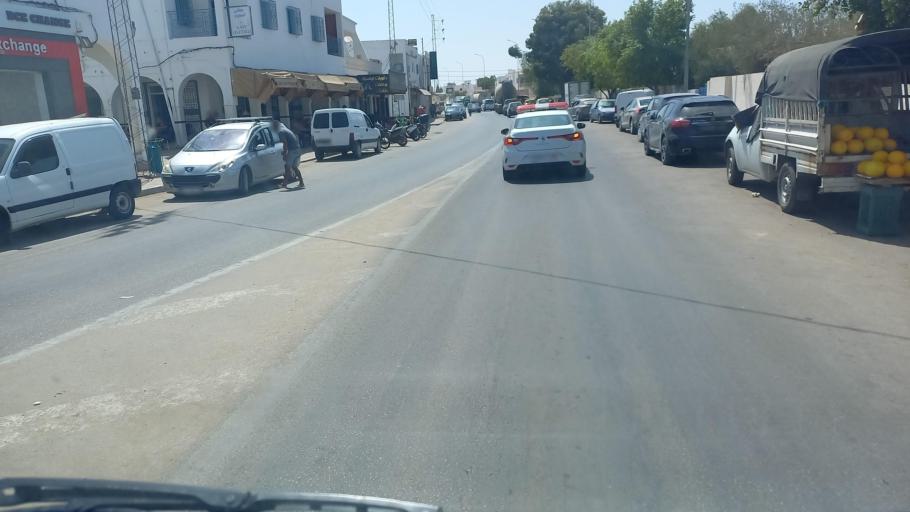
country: TN
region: Madanin
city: Houmt Souk
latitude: 33.8009
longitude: 10.8832
